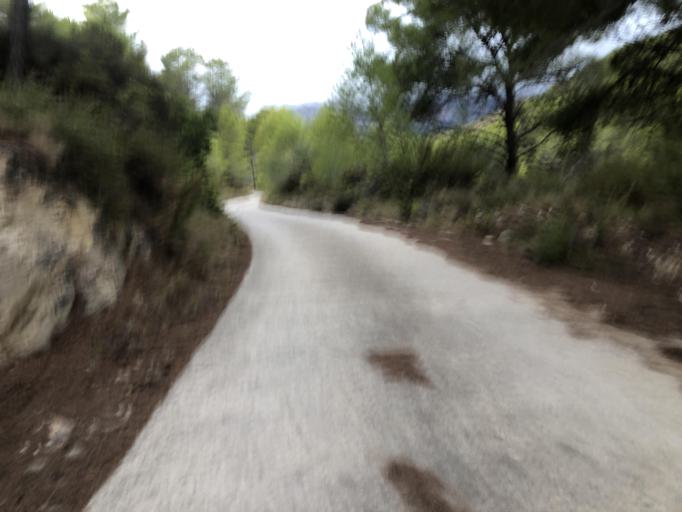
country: ES
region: Valencia
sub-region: Provincia de Alicante
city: Polop
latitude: 38.6389
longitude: -0.1387
